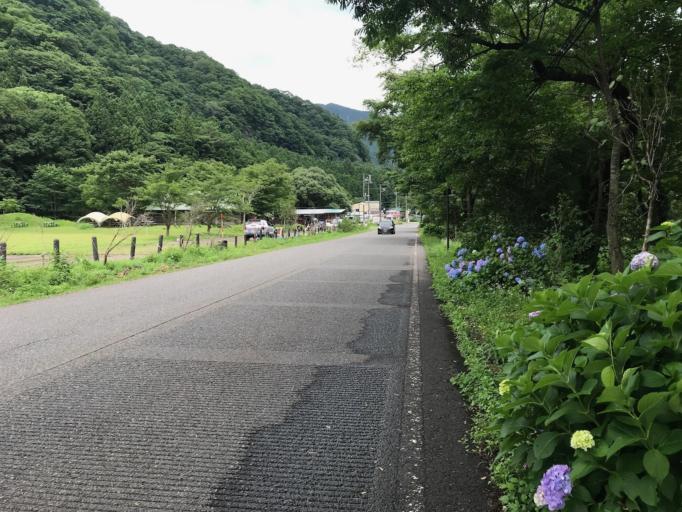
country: JP
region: Gunma
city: Numata
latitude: 36.8133
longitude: 138.9855
